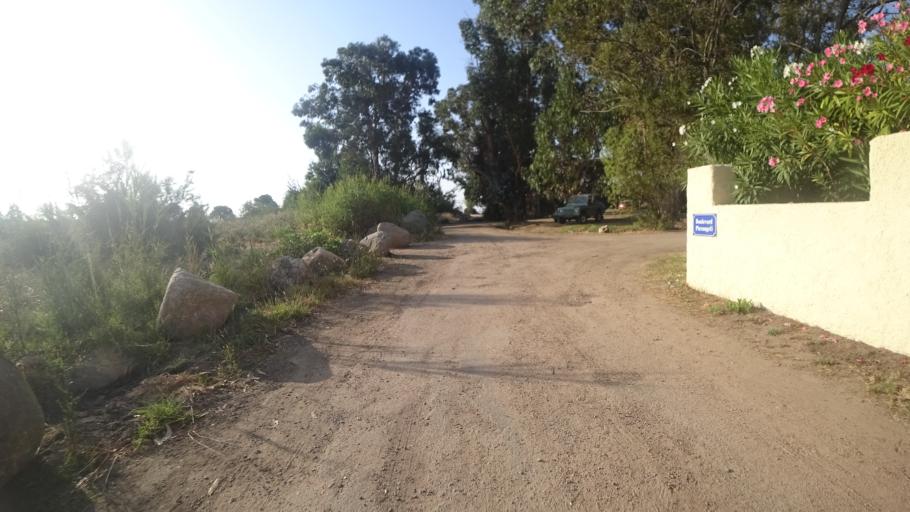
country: FR
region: Corsica
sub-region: Departement de la Corse-du-Sud
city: Porto-Vecchio
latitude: 41.6391
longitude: 9.3473
